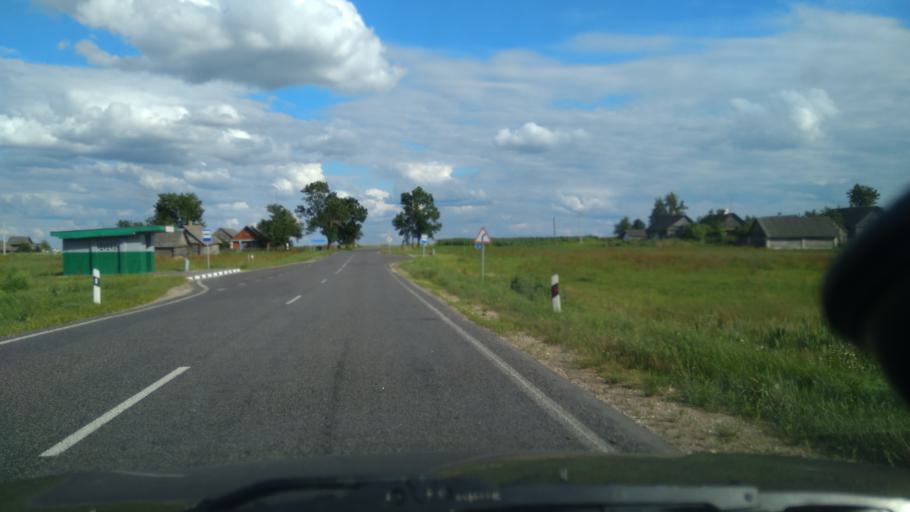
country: BY
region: Grodnenskaya
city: Masty
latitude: 53.3131
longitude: 24.6943
